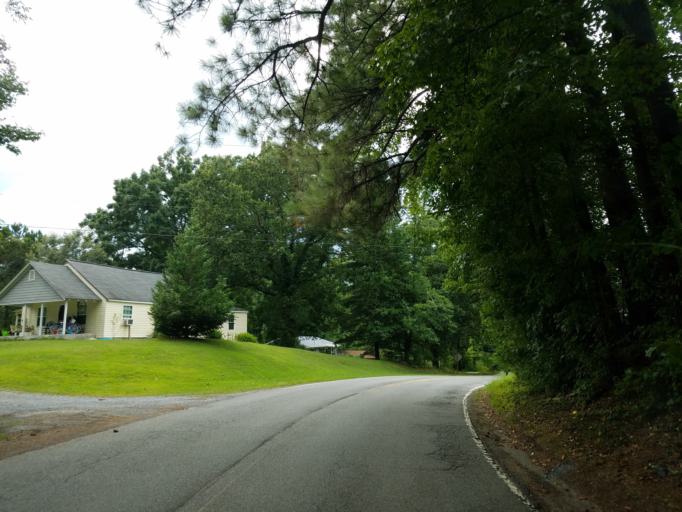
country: US
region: Georgia
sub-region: Bartow County
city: Rydal
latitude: 34.2704
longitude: -84.7534
